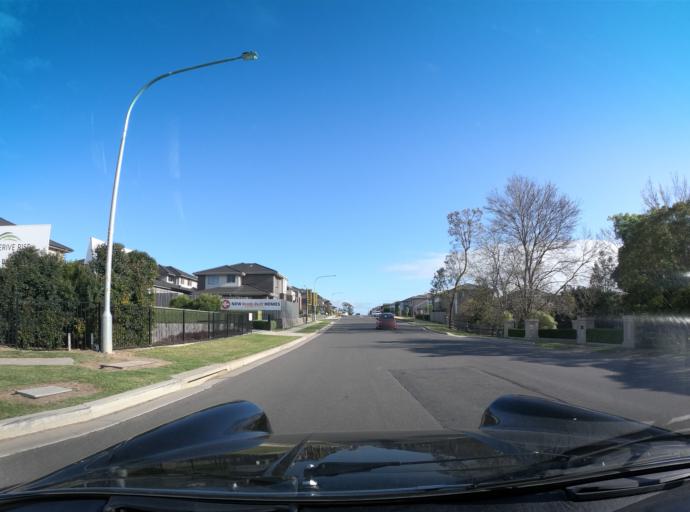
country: AU
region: New South Wales
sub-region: The Hills Shire
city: Beaumont Hills
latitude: -33.6957
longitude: 150.9632
